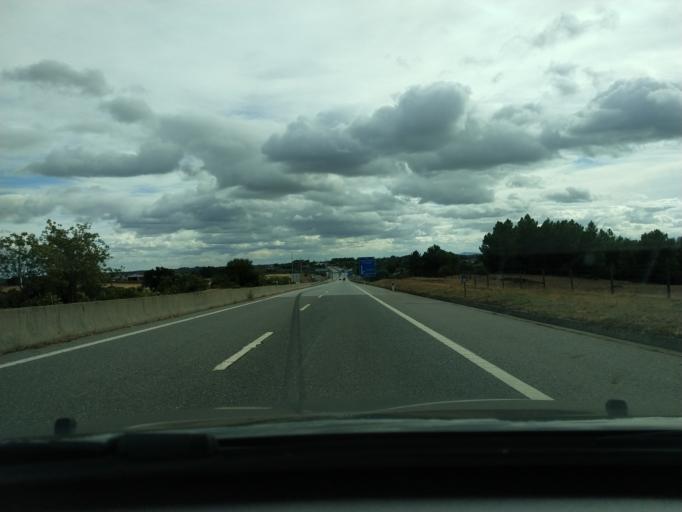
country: PT
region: Castelo Branco
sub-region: Concelho do Fundao
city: Fundao
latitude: 40.0396
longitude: -7.4697
